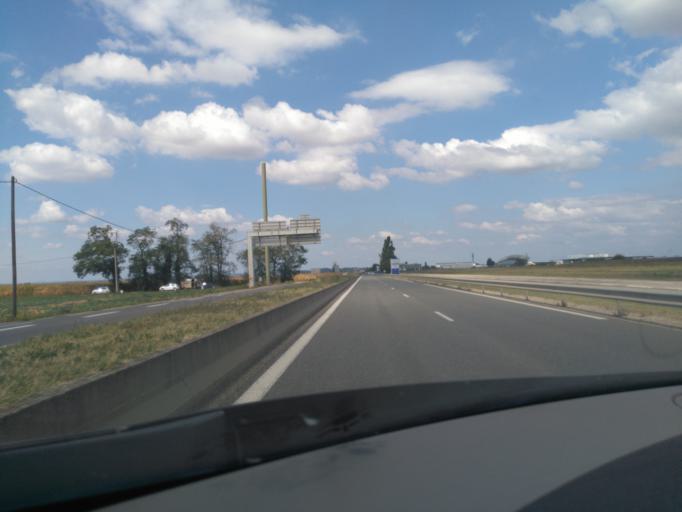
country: FR
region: Rhone-Alpes
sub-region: Departement du Rhone
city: Saint-Laurent-de-Mure
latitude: 45.7045
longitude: 5.0719
